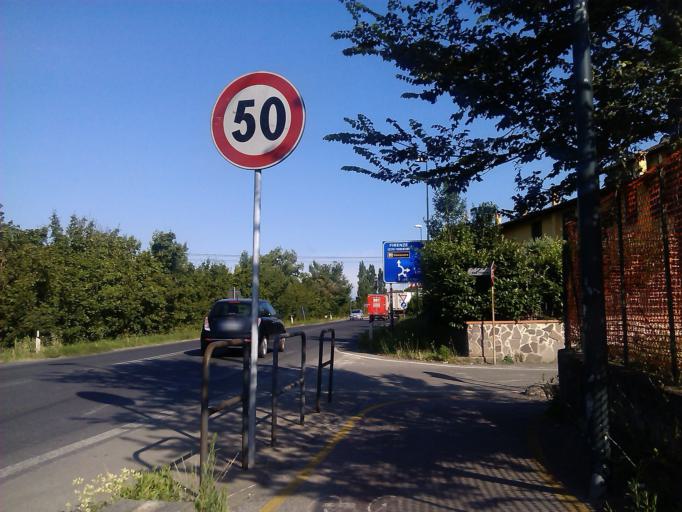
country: IT
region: Tuscany
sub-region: Province of Florence
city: Campi Bisenzio
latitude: 43.8164
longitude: 11.1527
